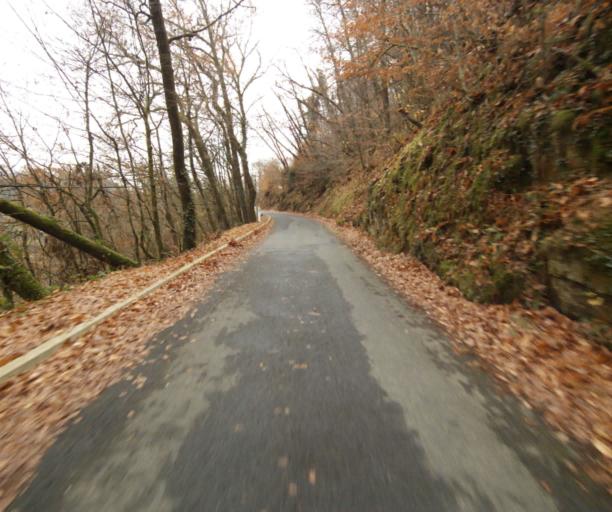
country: FR
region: Limousin
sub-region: Departement de la Correze
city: Chameyrat
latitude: 45.2412
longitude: 1.7324
